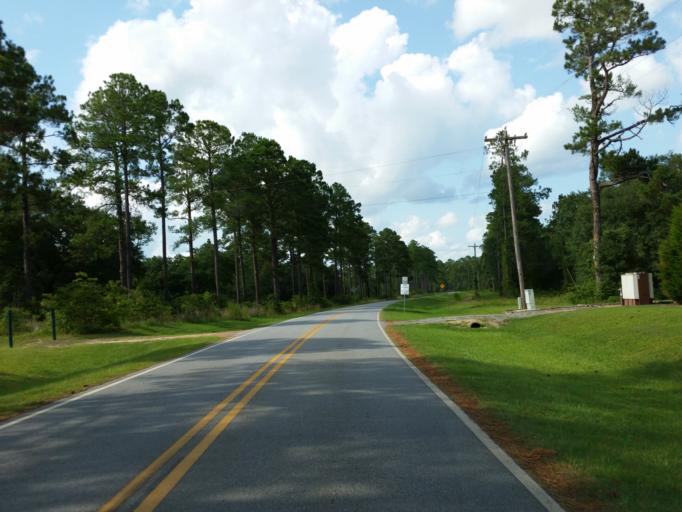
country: US
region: Georgia
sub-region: Lee County
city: Leesburg
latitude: 31.7271
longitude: -84.0470
